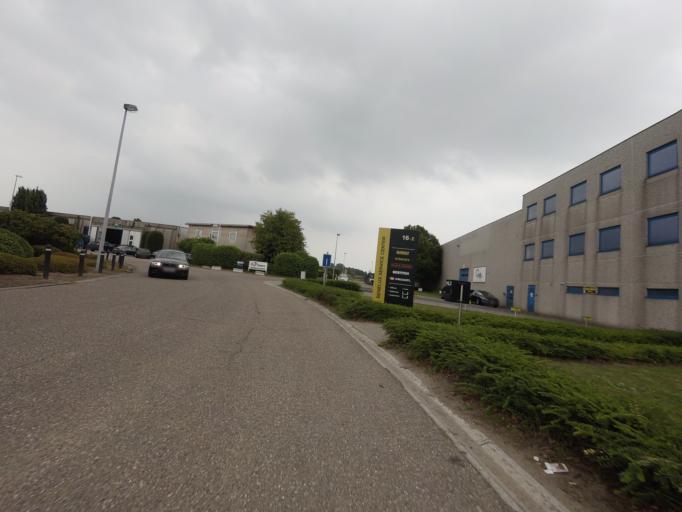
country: BE
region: Flanders
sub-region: Provincie Vlaams-Brabant
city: Boortmeerbeek
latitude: 50.9643
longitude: 4.5847
